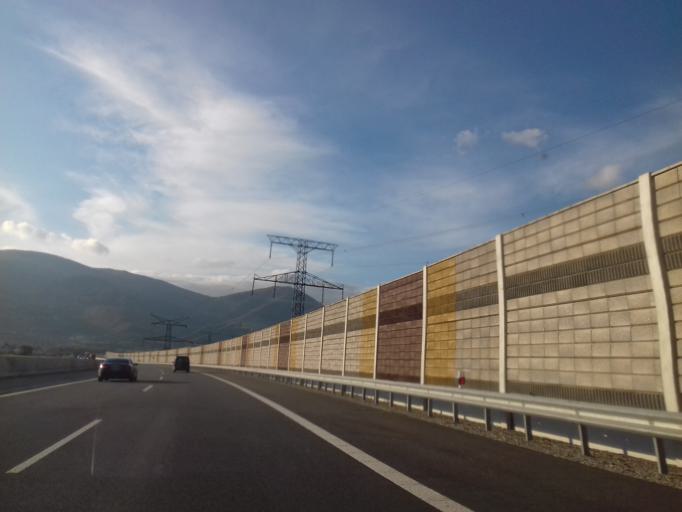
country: SK
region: Zilinsky
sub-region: Okres Zilina
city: Vrutky
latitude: 49.1210
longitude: 18.9340
